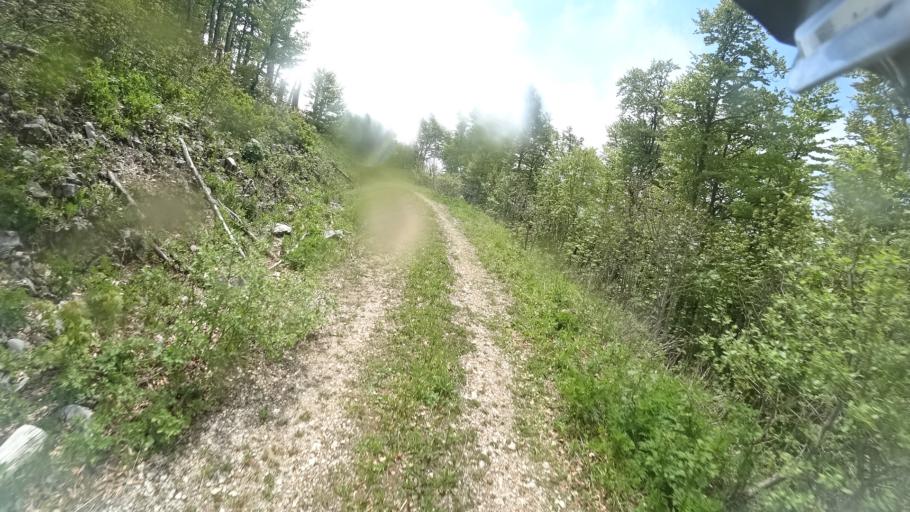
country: BA
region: Federation of Bosnia and Herzegovina
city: Orasac
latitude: 44.5697
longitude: 15.8725
